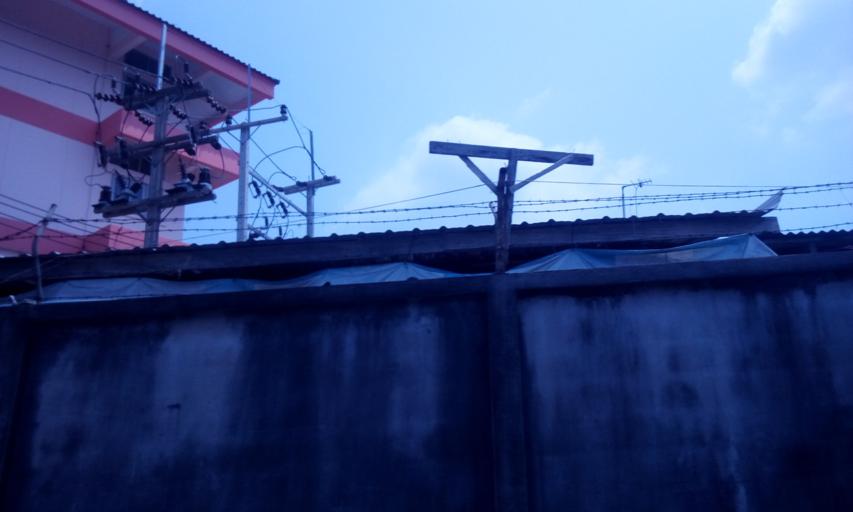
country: TH
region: Chachoengsao
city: Chachoengsao
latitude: 13.6924
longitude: 101.0755
